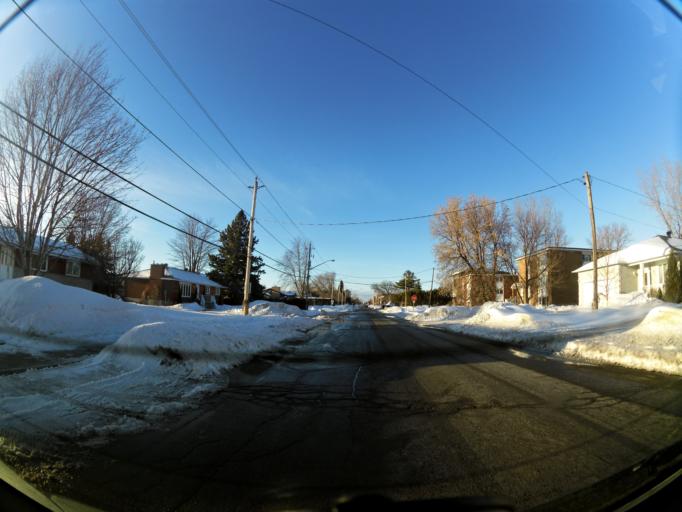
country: CA
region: Ontario
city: Ottawa
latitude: 45.4425
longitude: -75.5248
